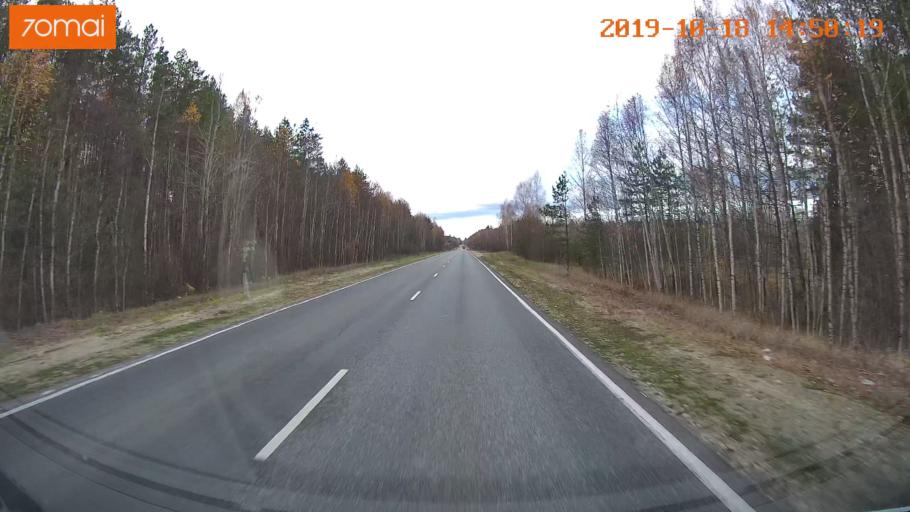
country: RU
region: Vladimir
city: Kurlovo
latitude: 55.4254
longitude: 40.6425
